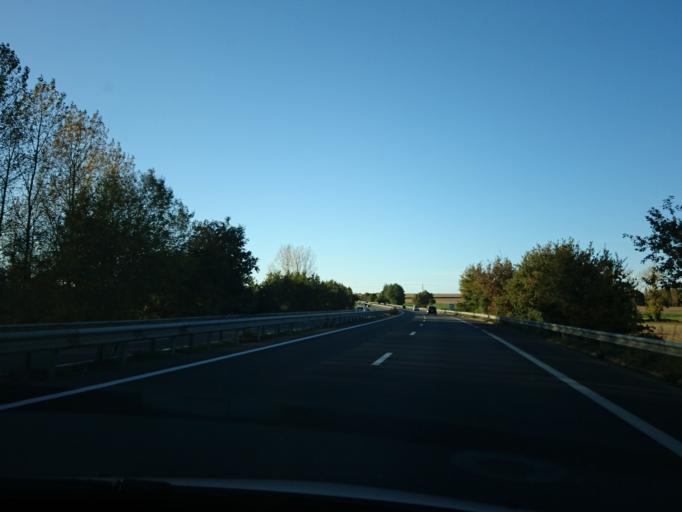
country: FR
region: Brittany
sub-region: Departement des Cotes-d'Armor
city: Broons
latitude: 48.3352
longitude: -2.2689
